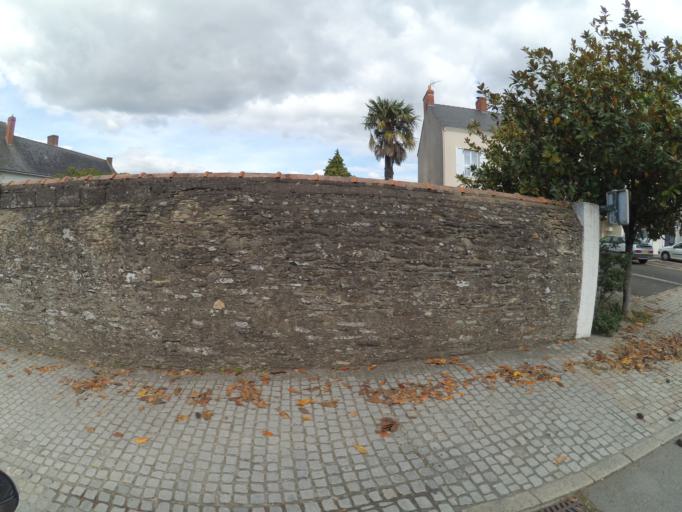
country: FR
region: Pays de la Loire
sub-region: Departement de la Loire-Atlantique
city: Carquefou
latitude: 47.2974
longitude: -1.4954
